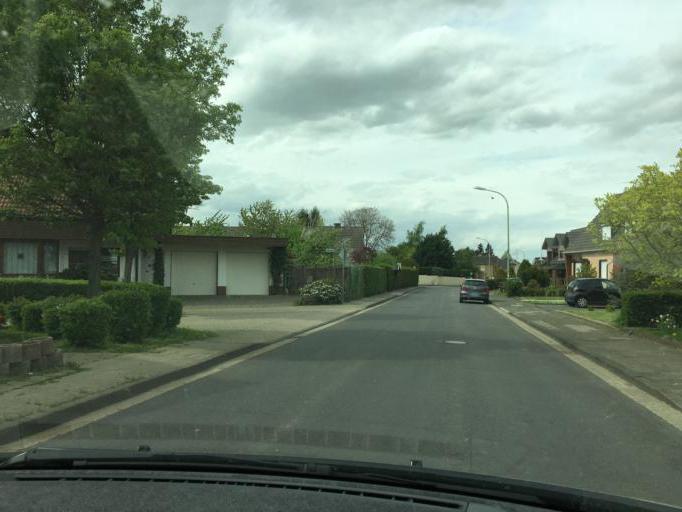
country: DE
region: North Rhine-Westphalia
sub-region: Regierungsbezirk Koln
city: Merzenich
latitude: 50.7811
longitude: 6.5535
